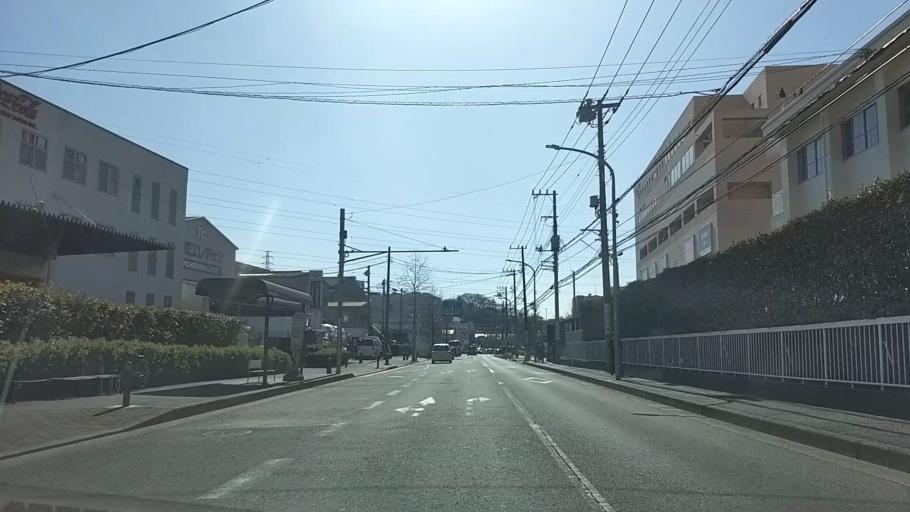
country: JP
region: Kanagawa
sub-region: Kawasaki-shi
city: Kawasaki
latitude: 35.5269
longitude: 139.6470
